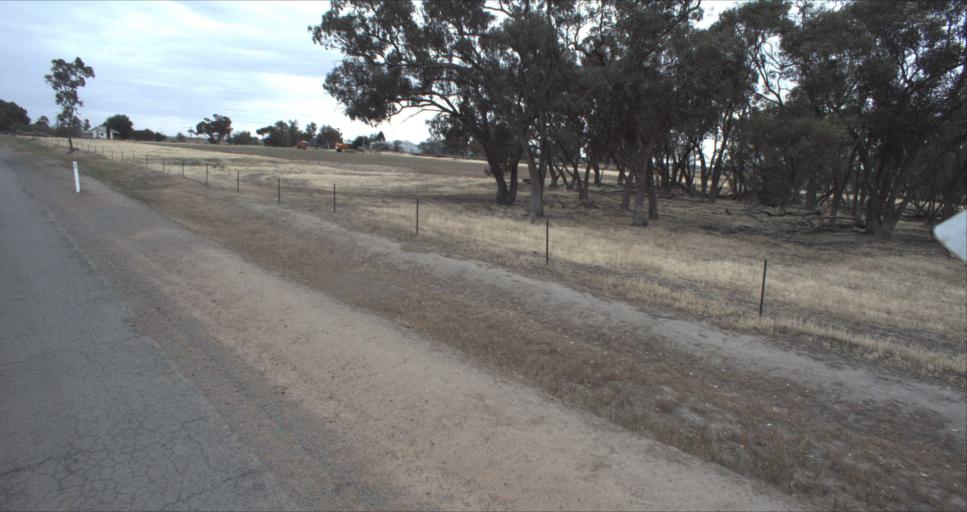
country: AU
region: New South Wales
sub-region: Leeton
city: Leeton
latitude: -34.4089
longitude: 146.3407
